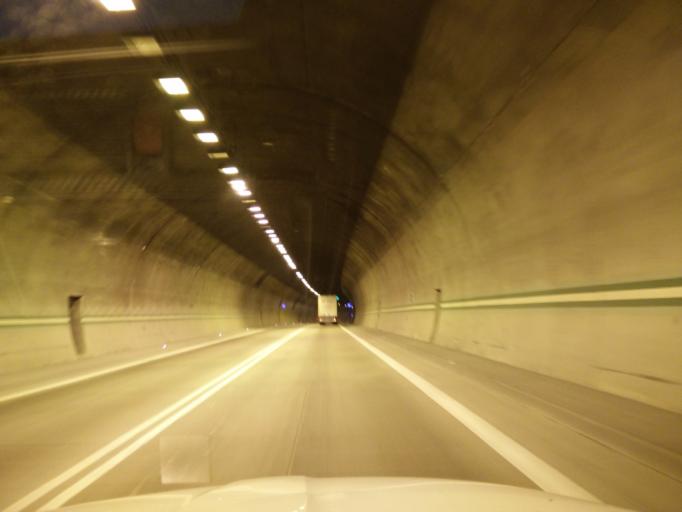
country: SK
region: Zilinsky
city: Cadca
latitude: 49.4321
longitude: 18.8082
